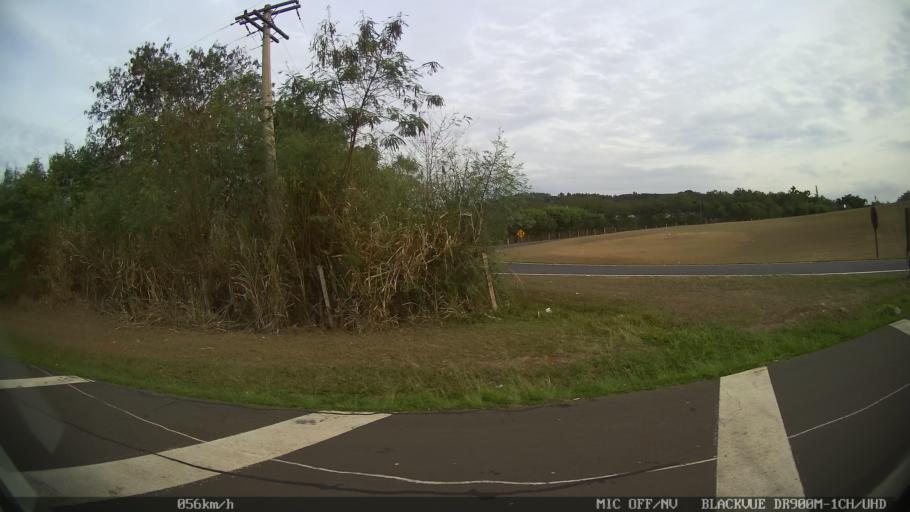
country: BR
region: Sao Paulo
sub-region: Piracicaba
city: Piracicaba
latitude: -22.7001
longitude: -47.6024
